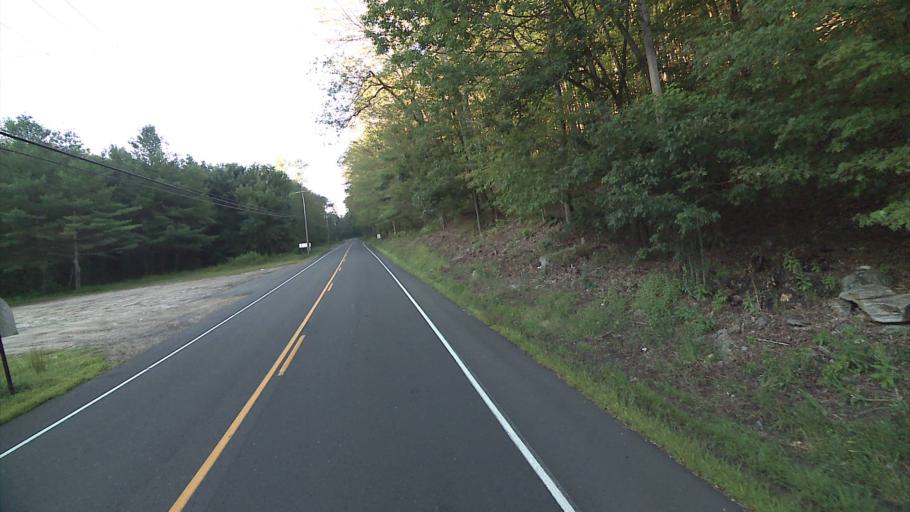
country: US
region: Connecticut
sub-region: Tolland County
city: Stafford Springs
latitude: 41.9455
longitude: -72.3050
